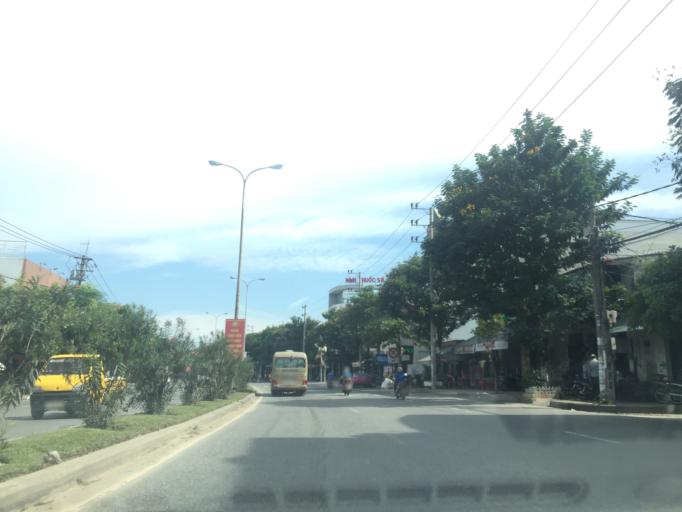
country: VN
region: Da Nang
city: Lien Chieu
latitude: 16.0677
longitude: 108.1522
